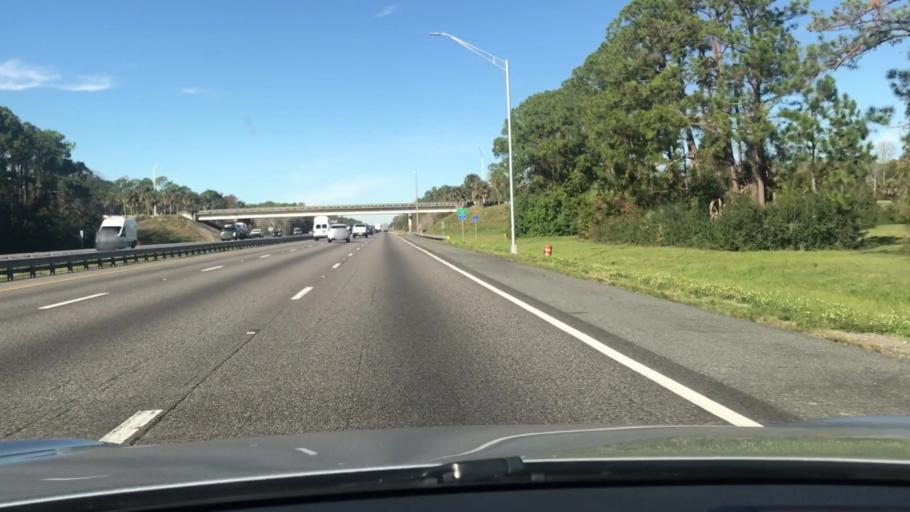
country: US
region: Florida
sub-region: Flagler County
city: Flagler Beach
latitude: 29.4023
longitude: -81.1543
